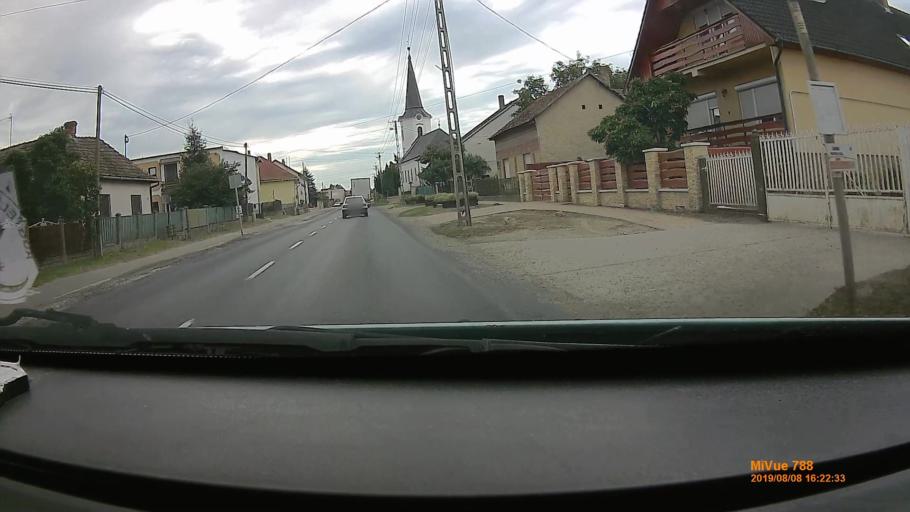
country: HU
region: Szabolcs-Szatmar-Bereg
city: Nyirmeggyes
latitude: 47.9707
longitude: 22.2502
